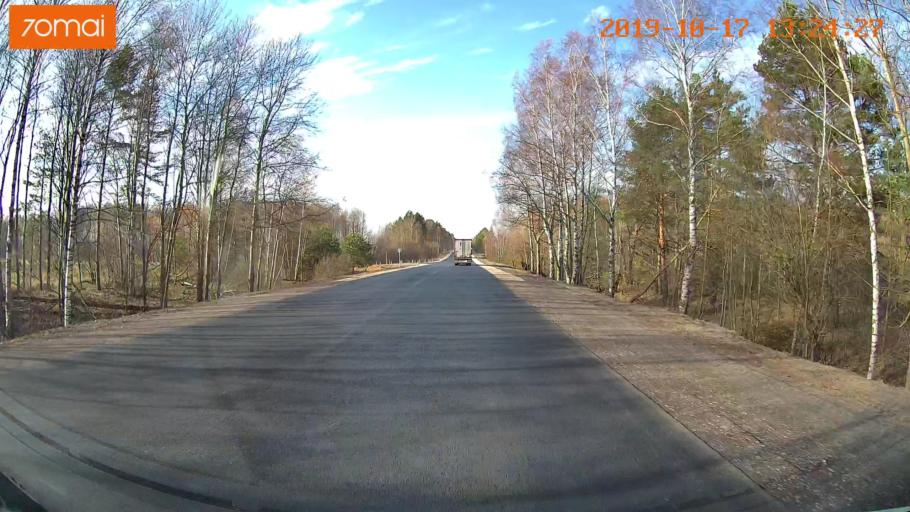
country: RU
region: Rjazan
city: Gus'-Zheleznyy
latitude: 55.0955
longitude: 40.9629
